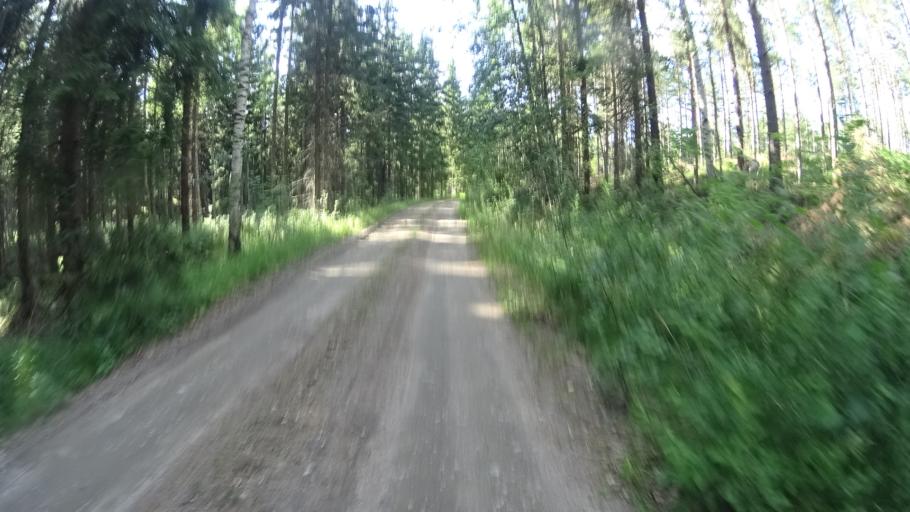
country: FI
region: Uusimaa
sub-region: Helsinki
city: Karkkila
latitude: 60.6381
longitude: 24.1626
